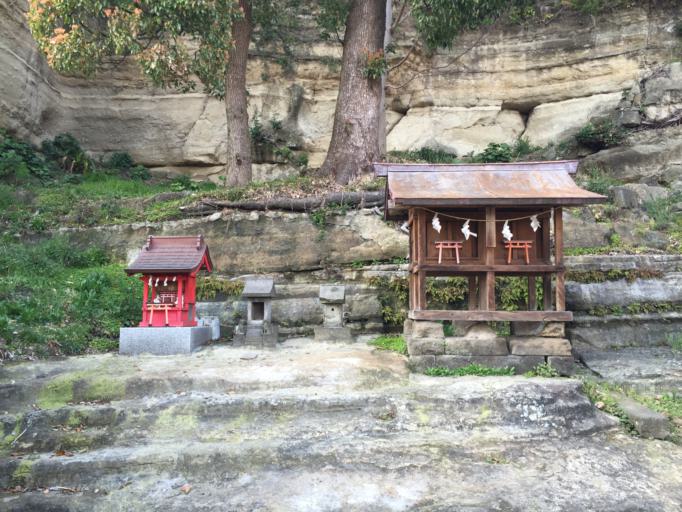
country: JP
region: Kanagawa
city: Zushi
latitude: 35.3325
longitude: 139.6218
